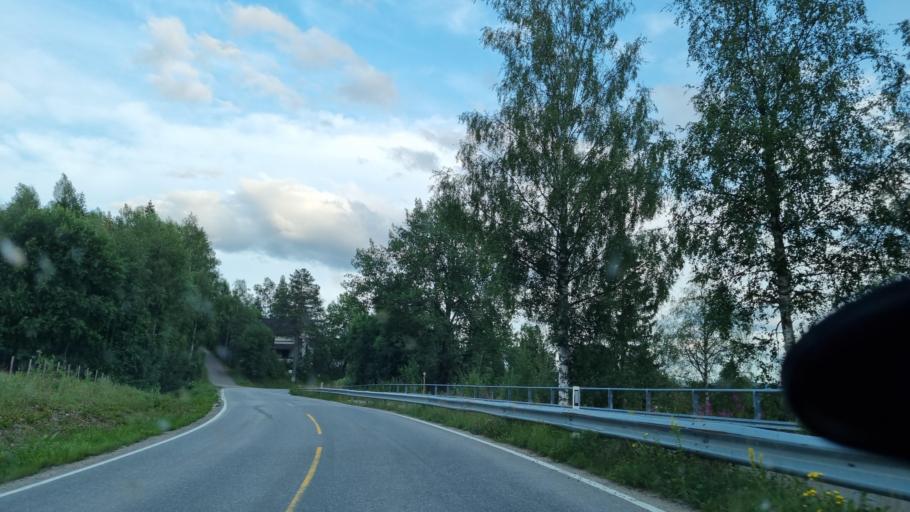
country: NO
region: Hedmark
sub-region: Trysil
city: Innbygda
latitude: 61.3056
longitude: 12.2730
